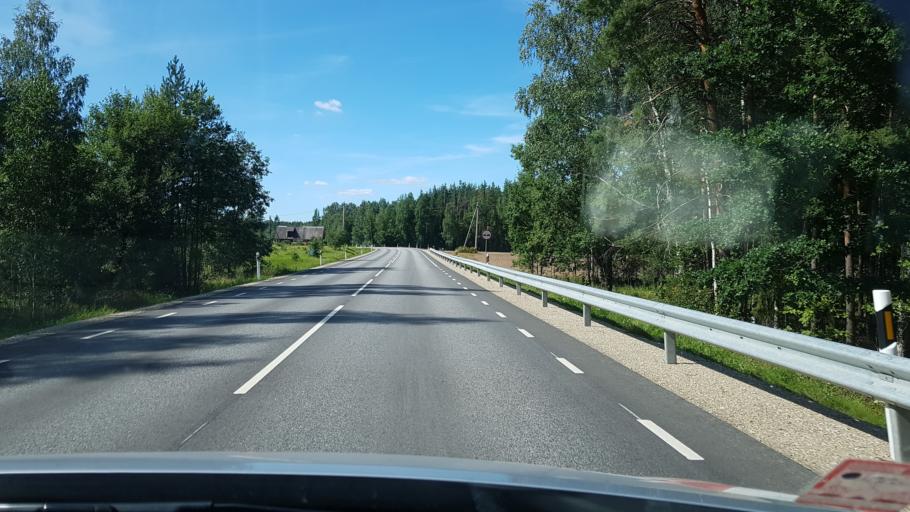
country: EE
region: Polvamaa
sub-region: Polva linn
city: Polva
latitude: 58.0394
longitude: 27.1229
